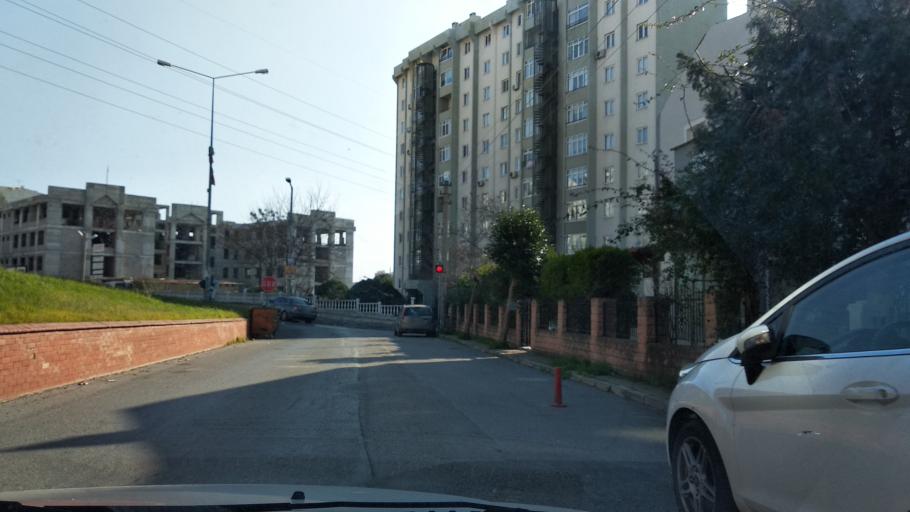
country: TR
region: Izmir
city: Karsiyaka
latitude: 38.4928
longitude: 27.0880
